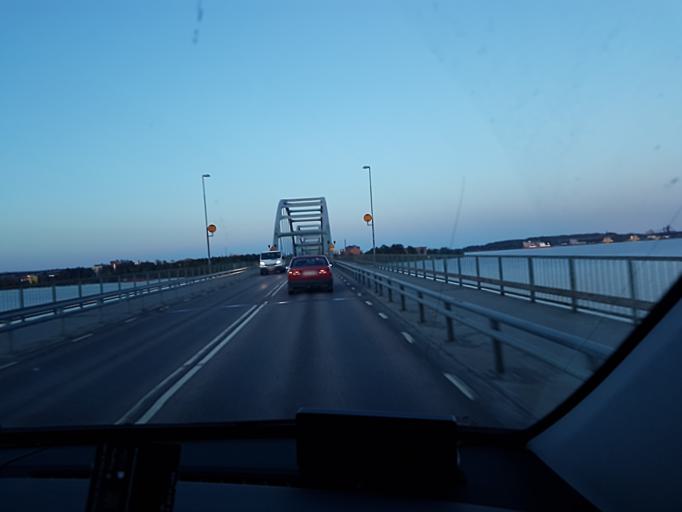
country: SE
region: Norrbotten
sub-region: Lulea Kommun
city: Bergnaset
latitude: 65.5779
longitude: 22.1143
